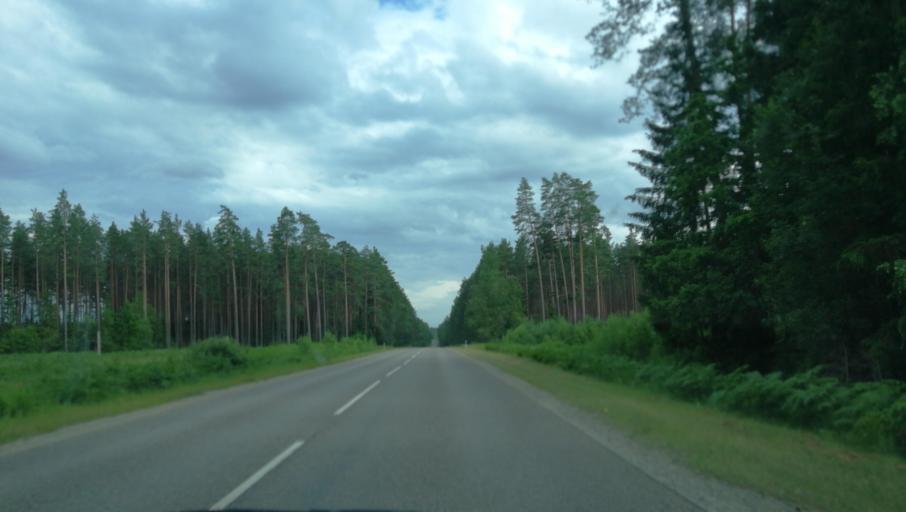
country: LV
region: Naukseni
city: Naukseni
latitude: 57.8115
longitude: 25.4060
